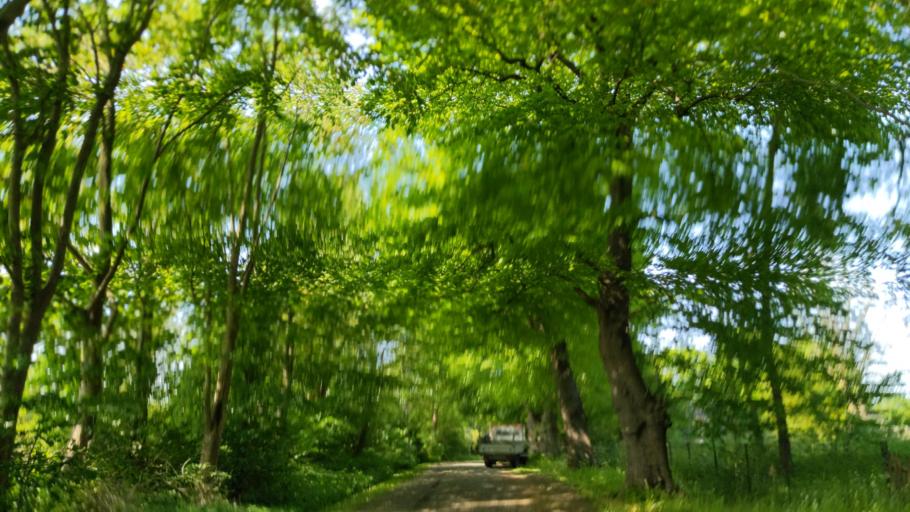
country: DE
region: Mecklenburg-Vorpommern
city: Selmsdorf
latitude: 53.8742
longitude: 10.8618
